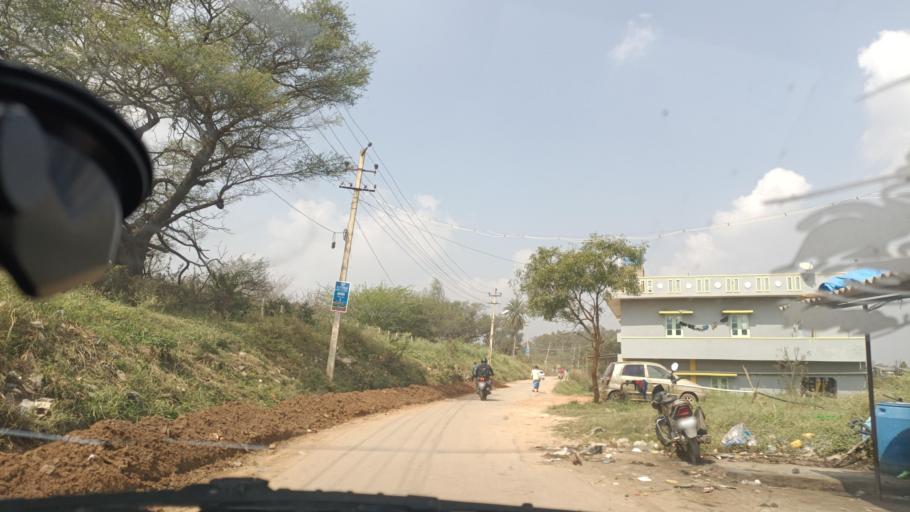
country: IN
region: Karnataka
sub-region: Bangalore Urban
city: Yelahanka
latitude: 13.1743
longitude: 77.6321
